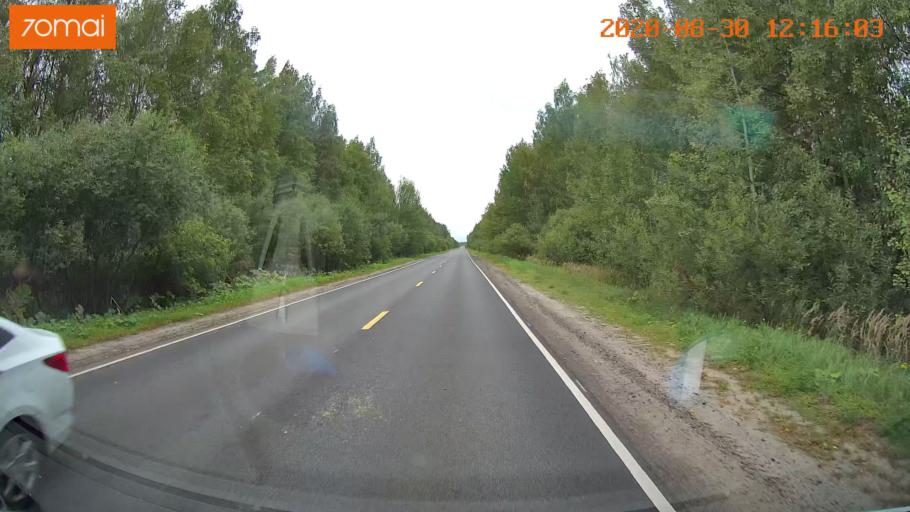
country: RU
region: Ivanovo
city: Yur'yevets
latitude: 57.3194
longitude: 43.0140
